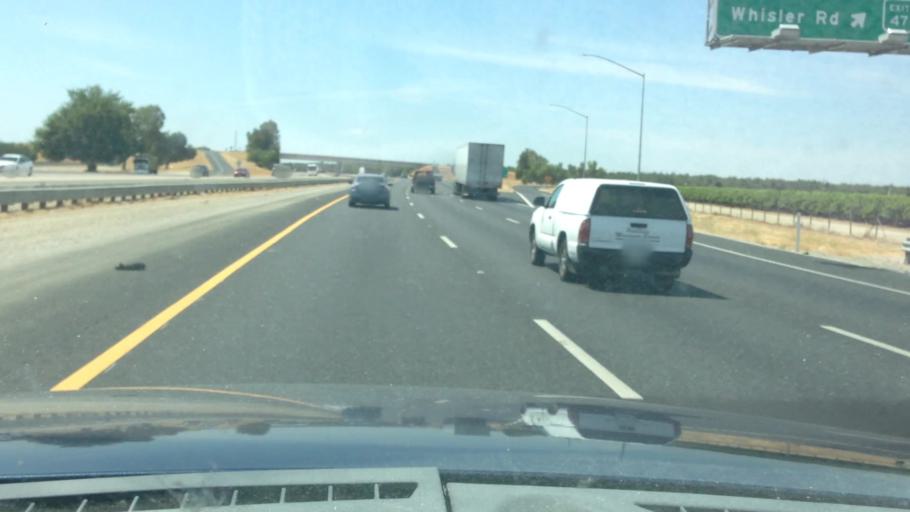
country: US
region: California
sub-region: Kern County
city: McFarland
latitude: 35.6499
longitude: -119.2209
